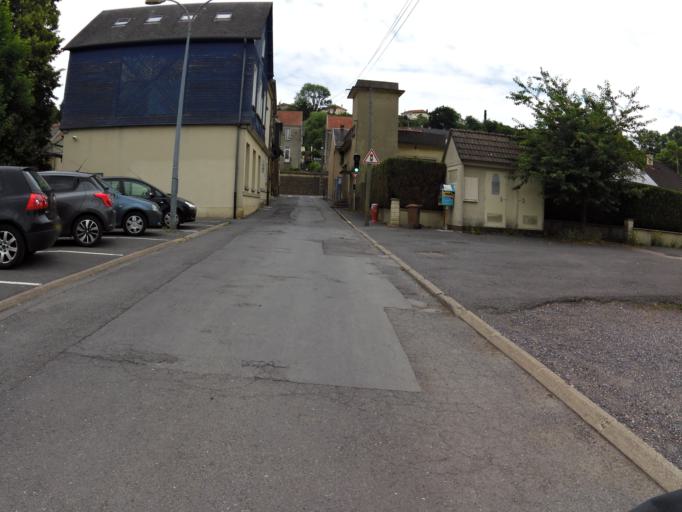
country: FR
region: Champagne-Ardenne
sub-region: Departement des Ardennes
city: Montcy-Notre-Dame
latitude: 49.7579
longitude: 4.7394
